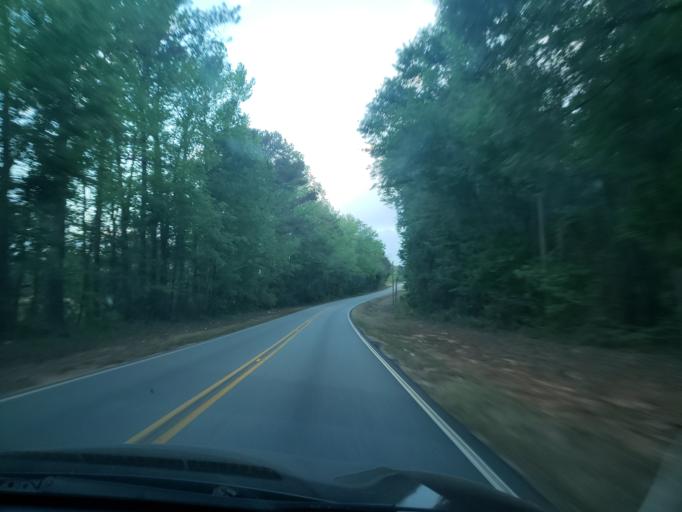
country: US
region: Alabama
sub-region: Tallapoosa County
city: Camp Hill
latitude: 32.6983
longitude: -85.6648
